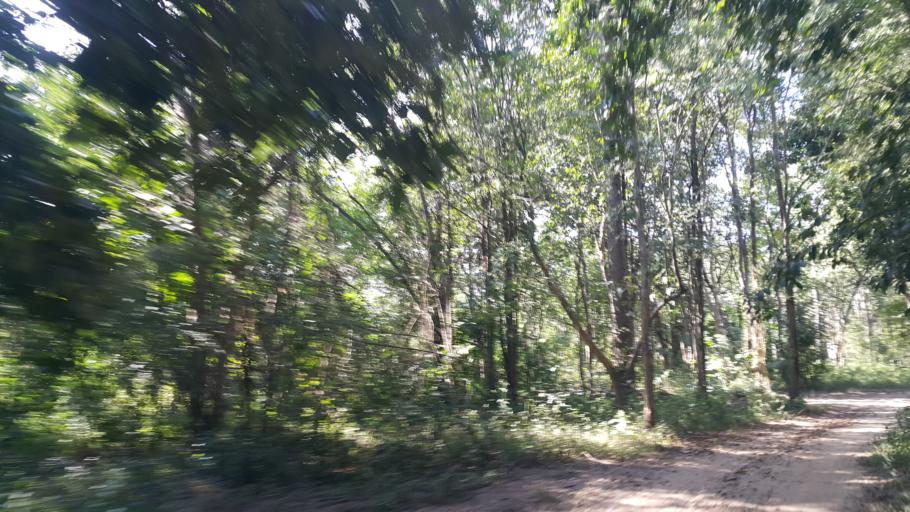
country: TH
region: Lamphun
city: Ban Thi
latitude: 18.5770
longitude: 99.1659
